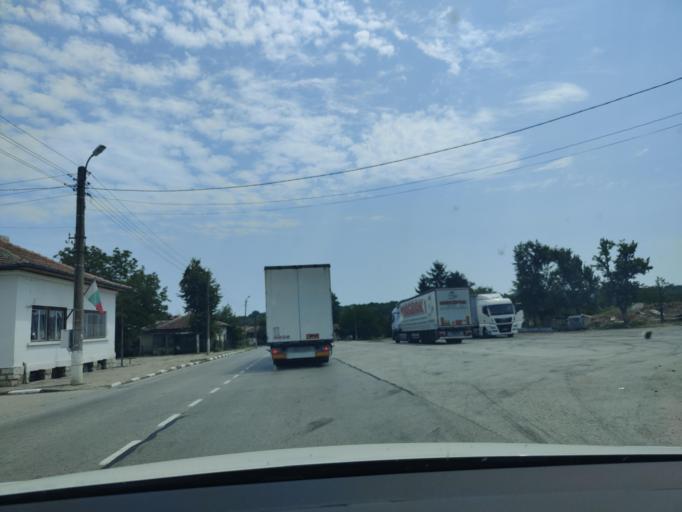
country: BG
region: Vidin
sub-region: Obshtina Ruzhintsi
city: Ruzhintsi
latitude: 43.6553
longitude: 22.7835
